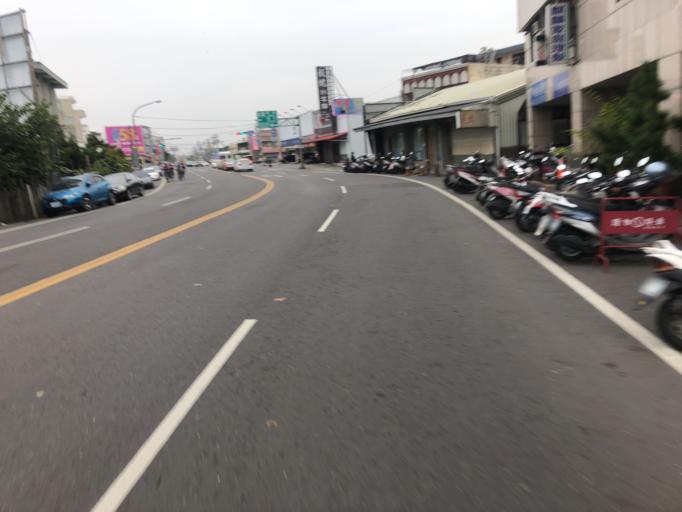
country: TW
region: Taiwan
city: Xinying
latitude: 23.1782
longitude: 120.2476
